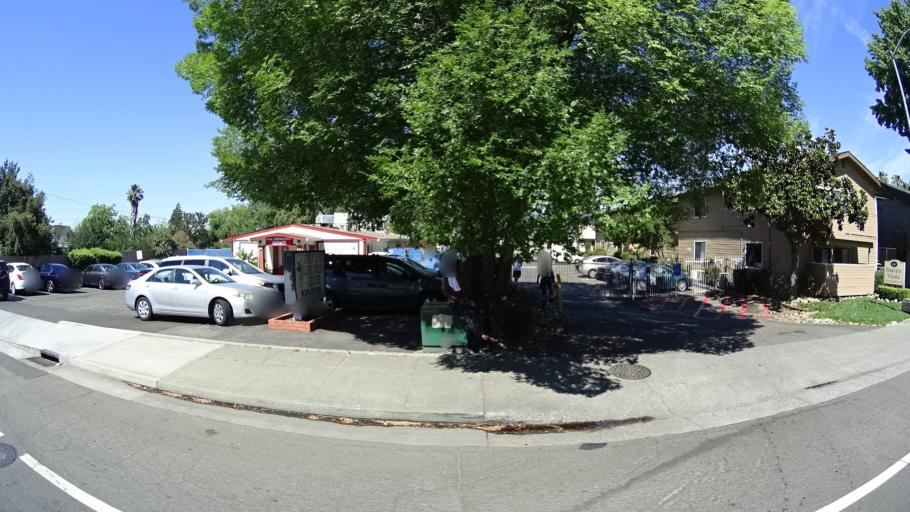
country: US
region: California
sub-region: Sacramento County
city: Arden-Arcade
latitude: 38.6128
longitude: -121.4154
